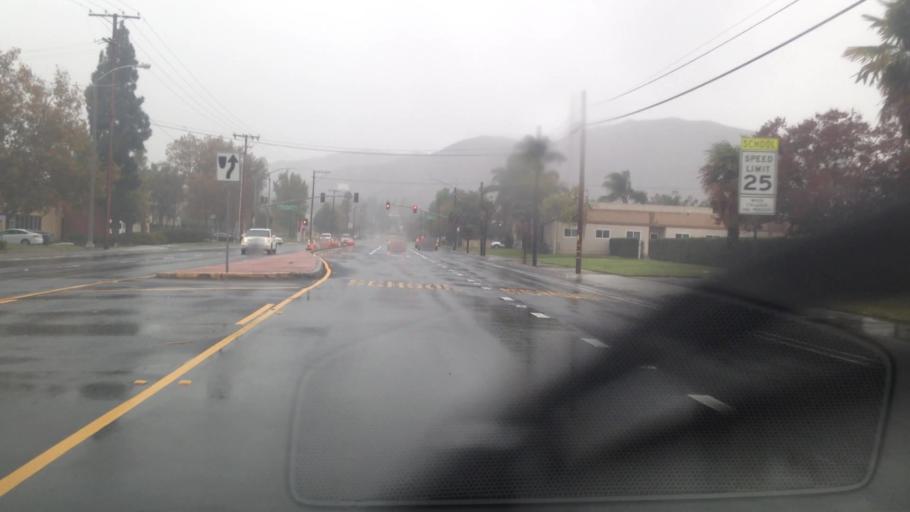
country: US
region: California
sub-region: Riverside County
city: Home Gardens
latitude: 33.9174
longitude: -117.4924
